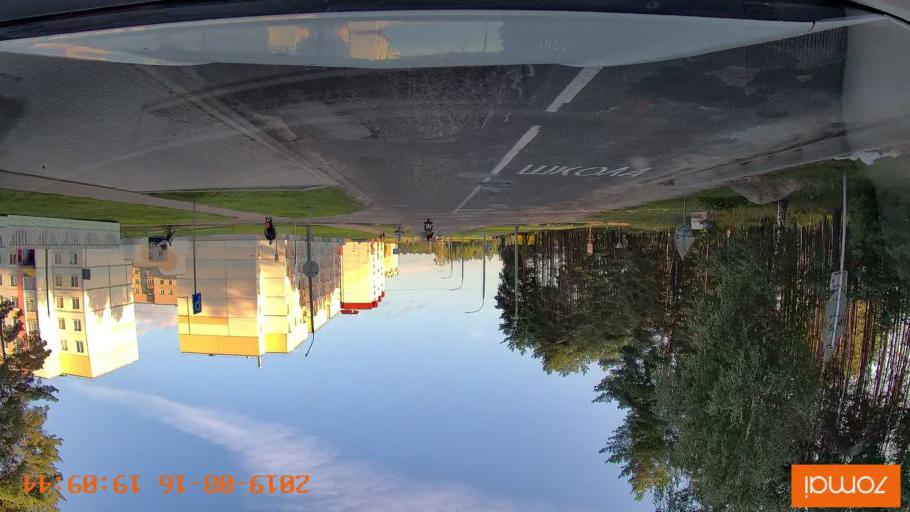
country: BY
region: Mogilev
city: Asipovichy
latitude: 53.3199
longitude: 28.6360
